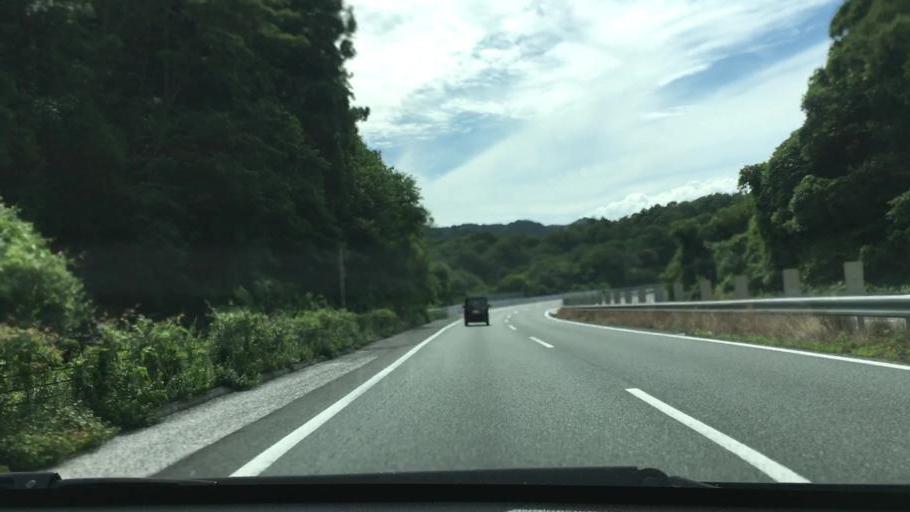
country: JP
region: Yamaguchi
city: Ogori-shimogo
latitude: 34.1266
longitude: 131.3863
